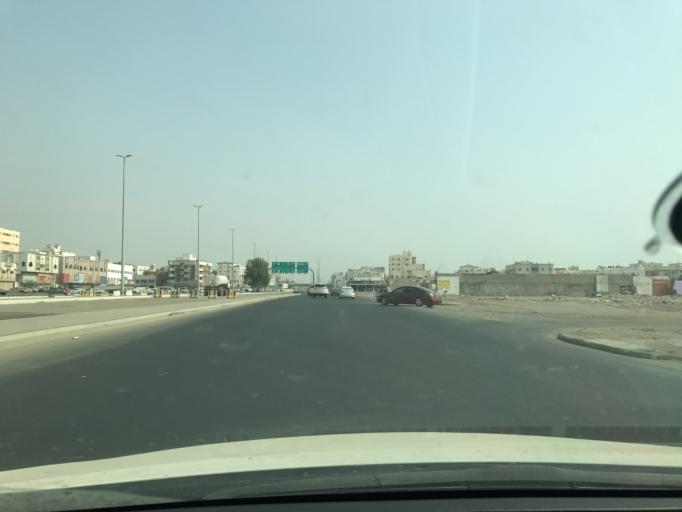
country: SA
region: Makkah
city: Jeddah
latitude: 21.6262
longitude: 39.1835
